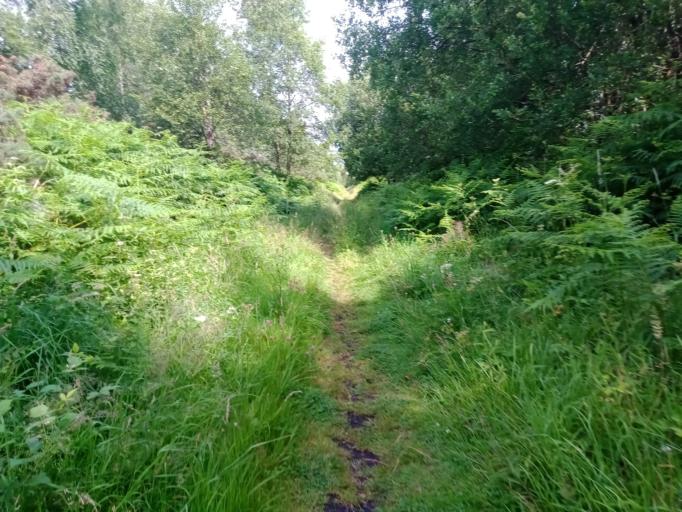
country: IE
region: Leinster
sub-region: Laois
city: Abbeyleix
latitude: 52.8911
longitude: -7.3503
